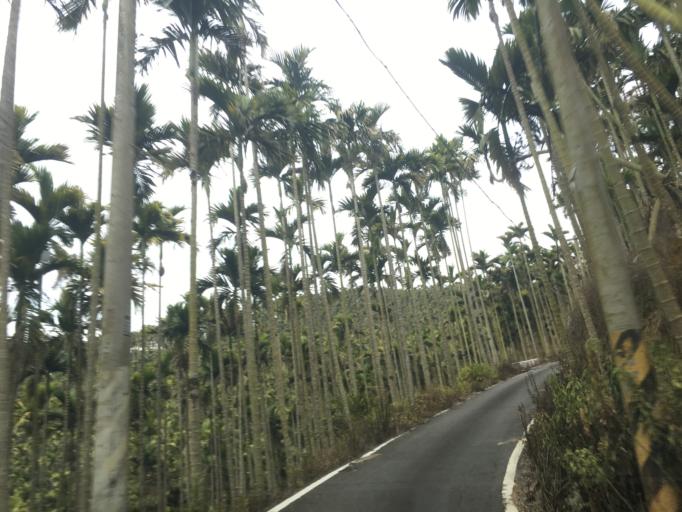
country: TW
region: Taiwan
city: Zhongxing New Village
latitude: 23.9696
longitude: 120.8270
